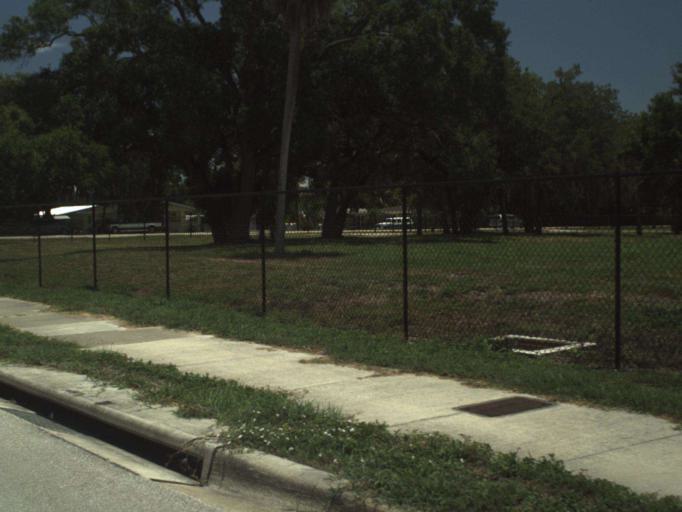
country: US
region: Florida
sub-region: Indian River County
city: Vero Beach
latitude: 27.6379
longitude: -80.3859
